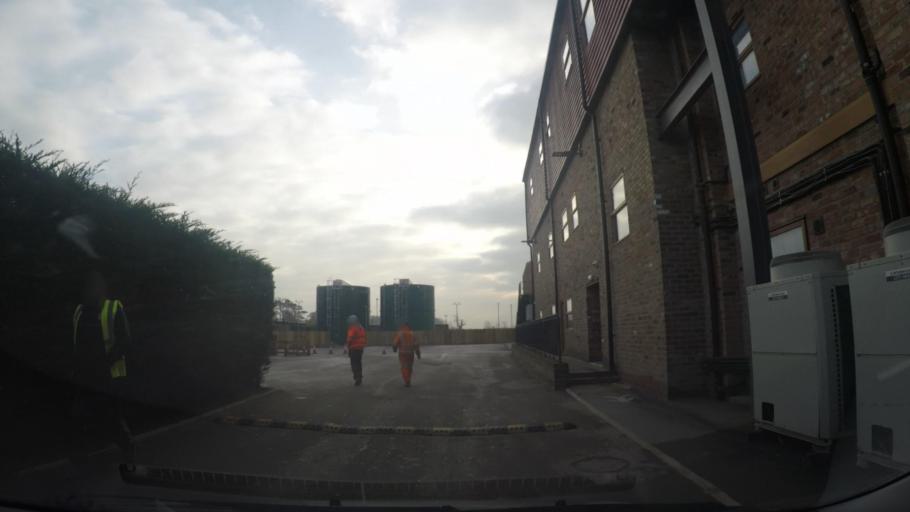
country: GB
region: England
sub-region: City and Borough of Leeds
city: Walton
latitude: 54.0274
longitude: -1.2911
